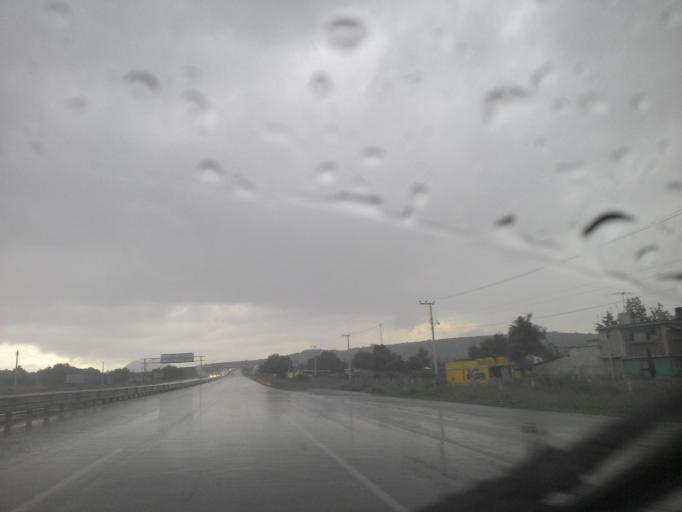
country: MX
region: Hidalgo
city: Zempoala
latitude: 19.8788
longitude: -98.6621
